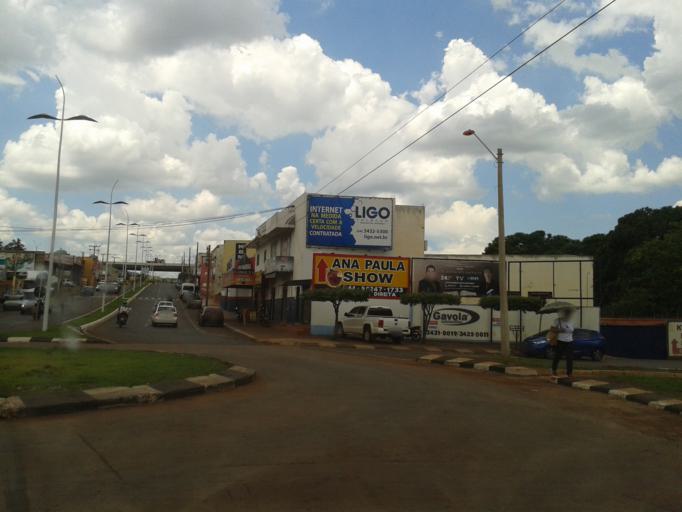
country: BR
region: Goias
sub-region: Itumbiara
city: Itumbiara
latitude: -18.4020
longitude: -49.2055
